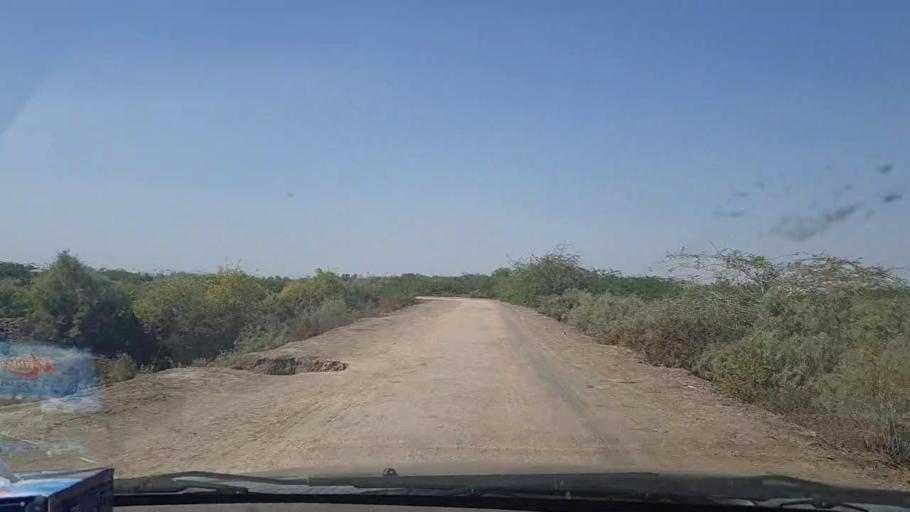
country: PK
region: Sindh
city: Chuhar Jamali
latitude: 24.2811
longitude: 67.7618
